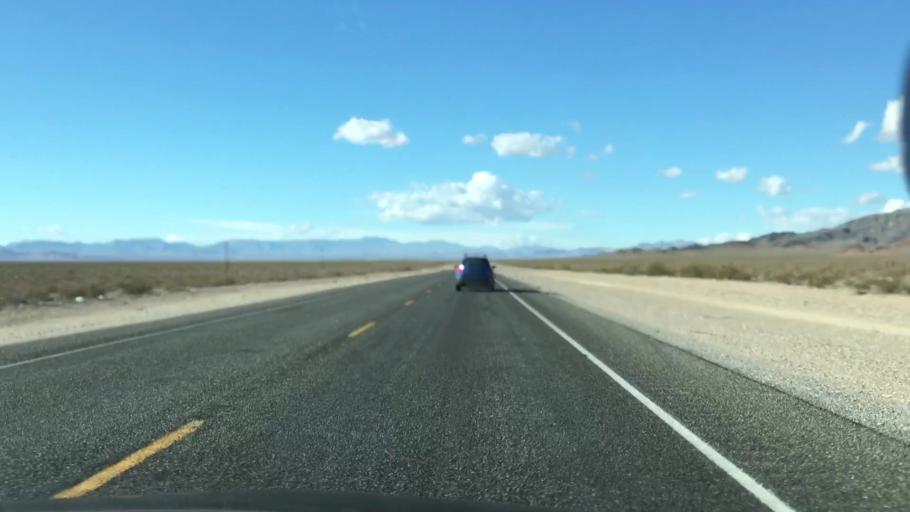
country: US
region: Nevada
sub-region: Nye County
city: Beatty
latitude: 36.7104
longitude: -116.5990
